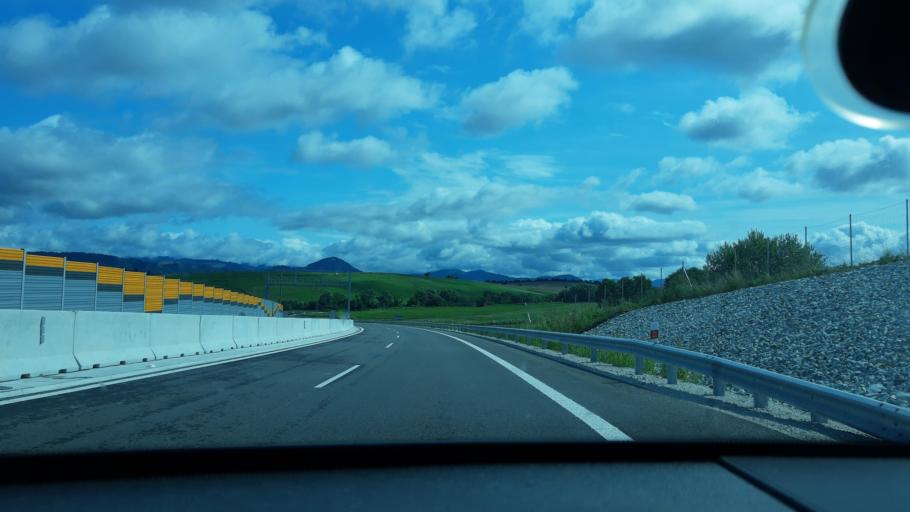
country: SK
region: Zilinsky
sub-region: Okres Zilina
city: Zilina
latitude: 49.1802
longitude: 18.7373
